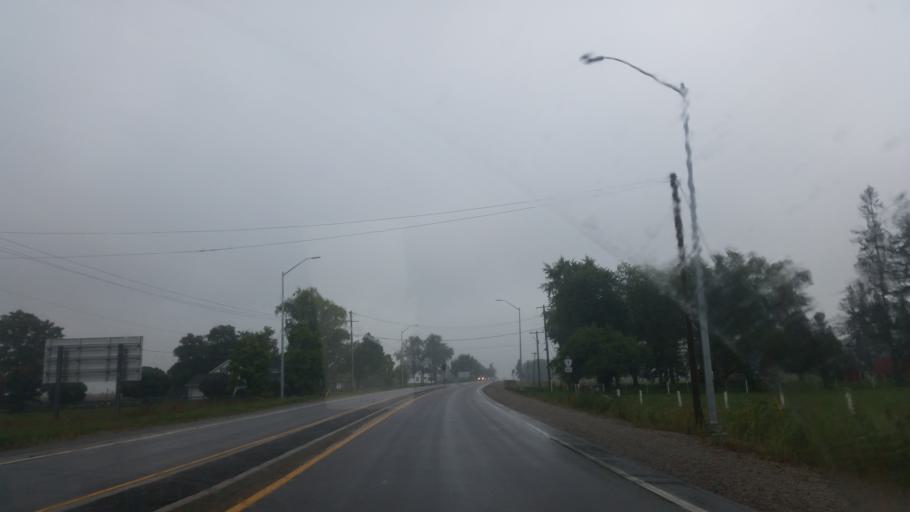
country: CA
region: Ontario
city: Stratford
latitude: 43.3081
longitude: -81.0361
